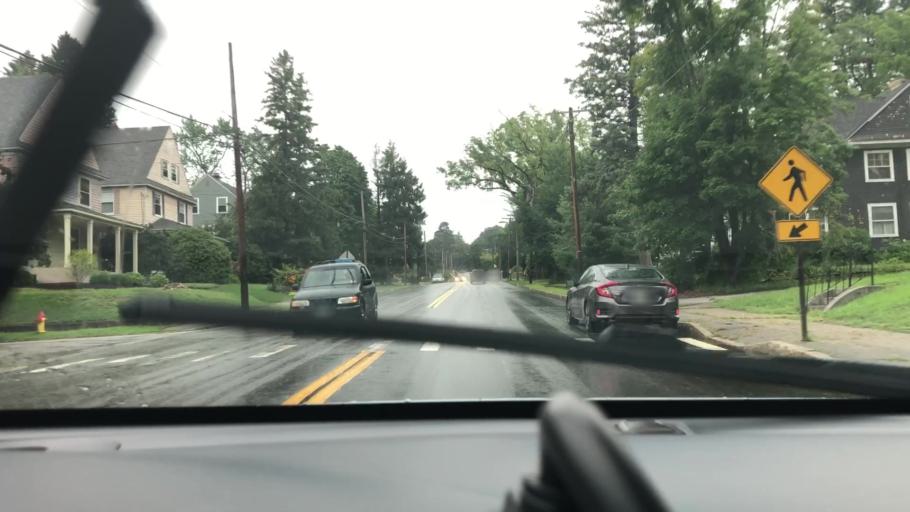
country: US
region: New Hampshire
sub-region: Hillsborough County
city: Manchester
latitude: 43.0101
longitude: -71.4607
